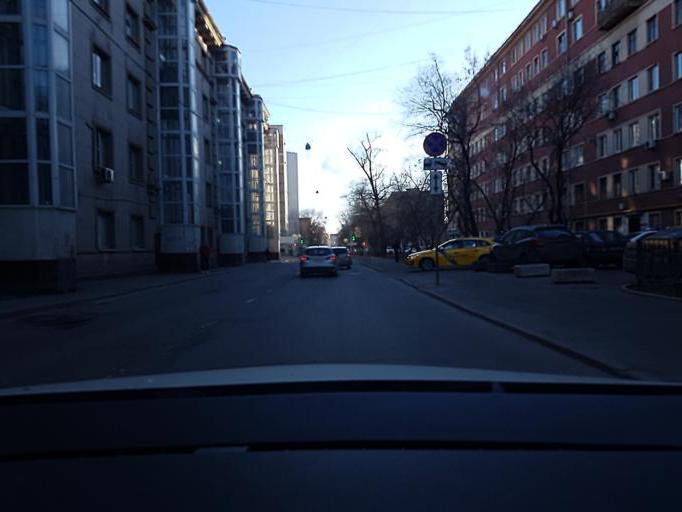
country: RU
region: Moskovskaya
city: Dorogomilovo
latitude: 55.7904
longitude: 37.5762
